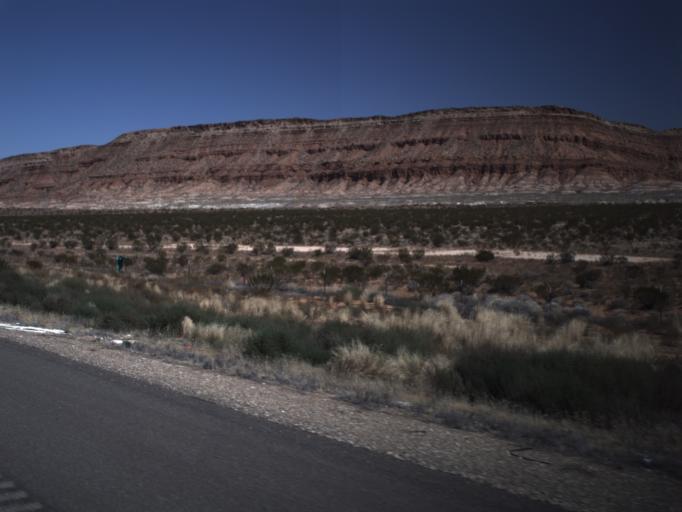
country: US
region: Utah
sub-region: Washington County
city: Washington
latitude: 37.0327
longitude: -113.4852
